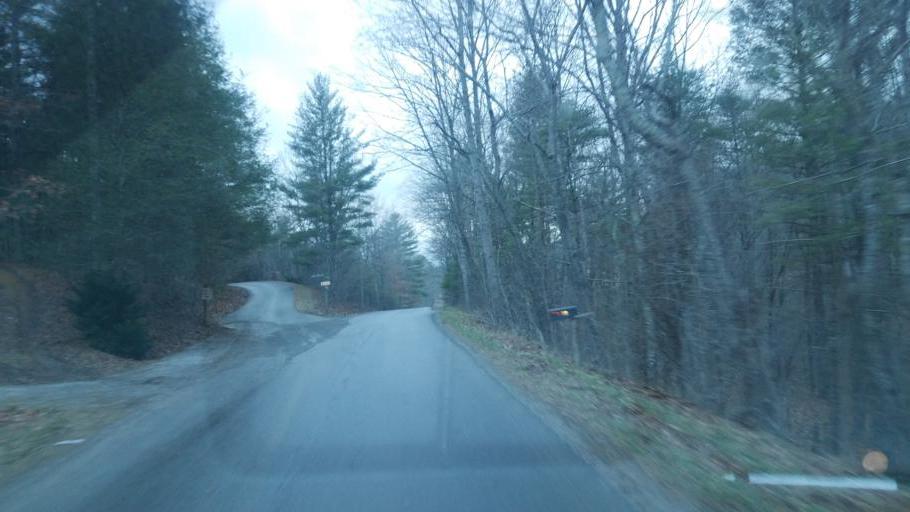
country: US
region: Virginia
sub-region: Pulaski County
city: Pulaski
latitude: 37.1812
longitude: -80.8479
